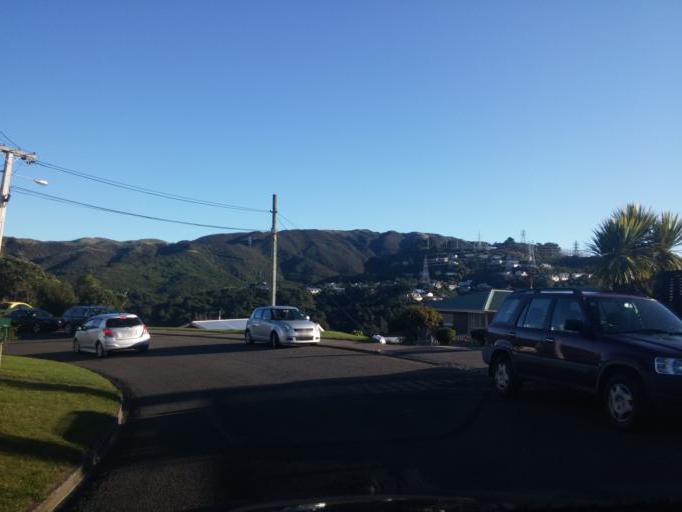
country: NZ
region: Wellington
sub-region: Wellington City
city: Kelburn
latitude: -41.2667
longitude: 174.7651
